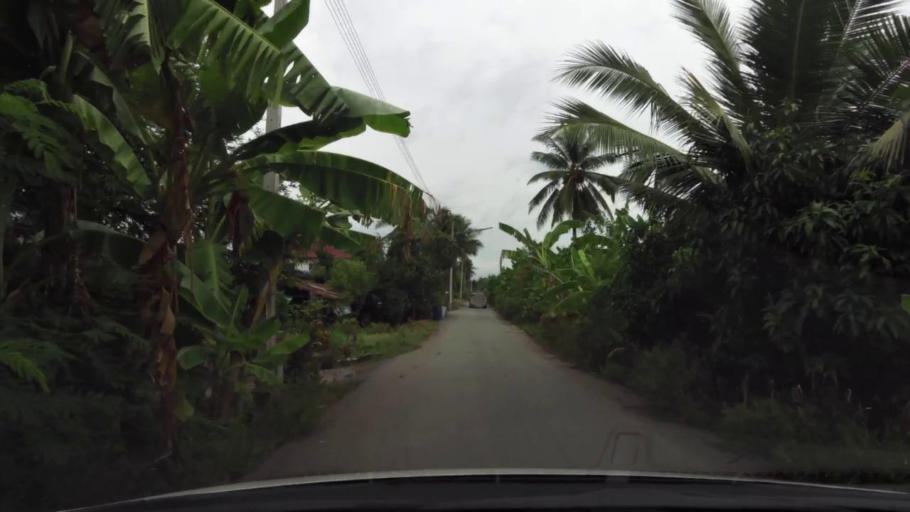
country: TH
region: Samut Sakhon
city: Ban Phaeo
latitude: 13.5980
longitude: 100.0293
